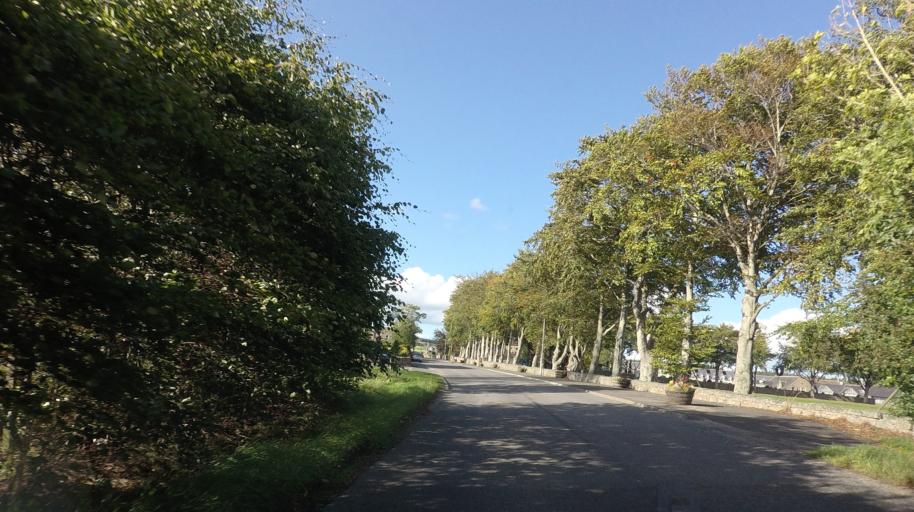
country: GB
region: Scotland
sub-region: Aberdeenshire
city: Kemnay
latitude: 57.1396
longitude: -2.4325
